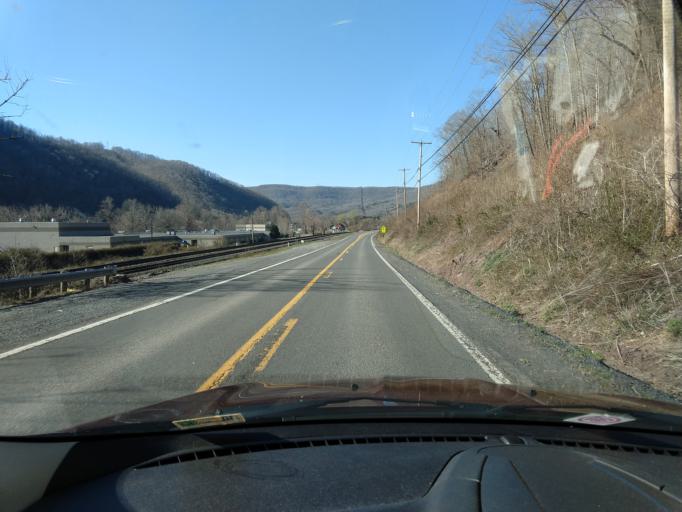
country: US
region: West Virginia
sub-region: Summers County
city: Hinton
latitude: 37.7050
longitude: -80.8867
